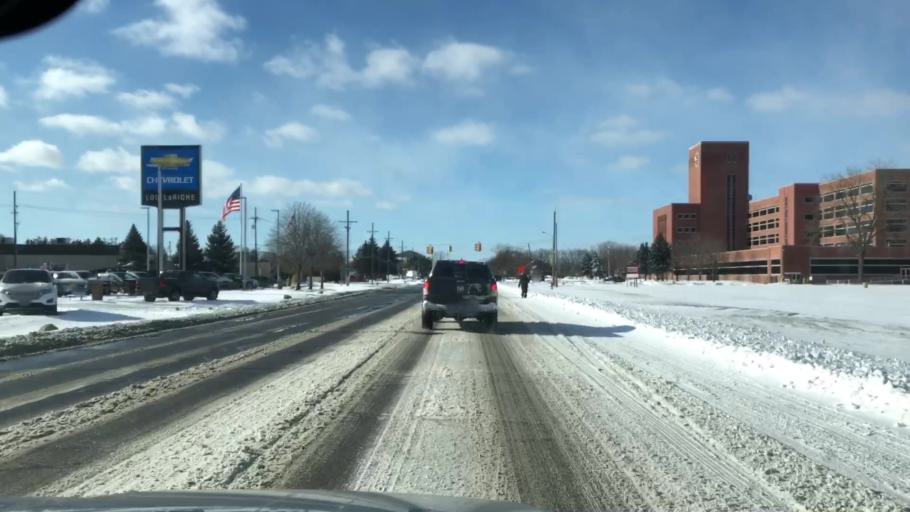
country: US
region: Michigan
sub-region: Wayne County
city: Plymouth
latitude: 42.3743
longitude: -83.4442
